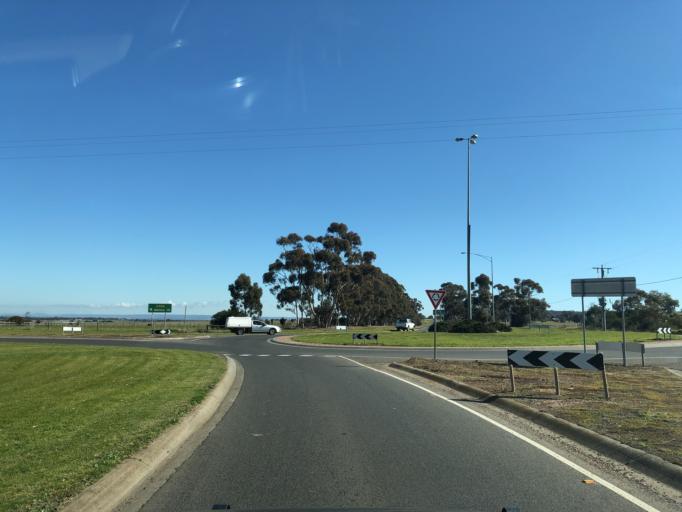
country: AU
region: Victoria
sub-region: Melton
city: Kurunjang
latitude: -37.6087
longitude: 144.5914
